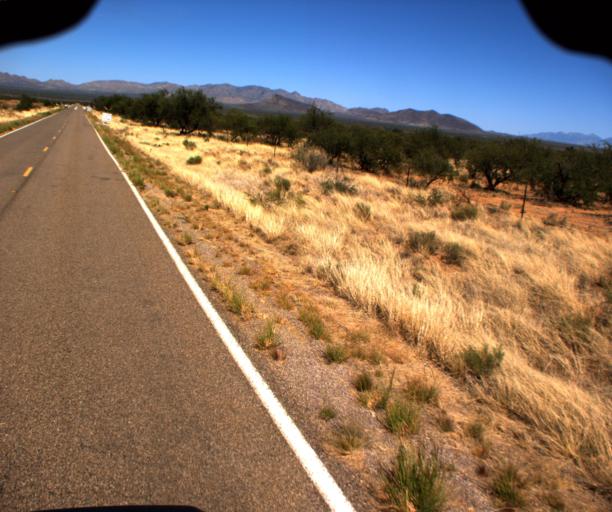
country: US
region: Arizona
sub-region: Pima County
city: Three Points
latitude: 31.8263
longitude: -111.4288
